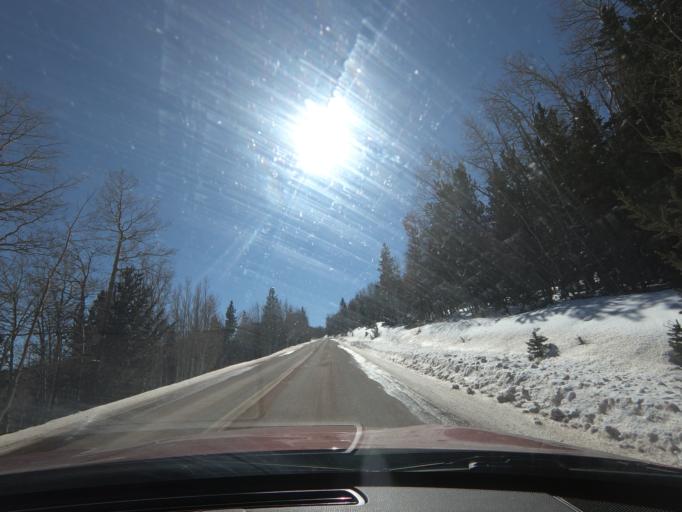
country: US
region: Colorado
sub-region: Teller County
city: Cripple Creek
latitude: 38.7384
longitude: -105.1207
